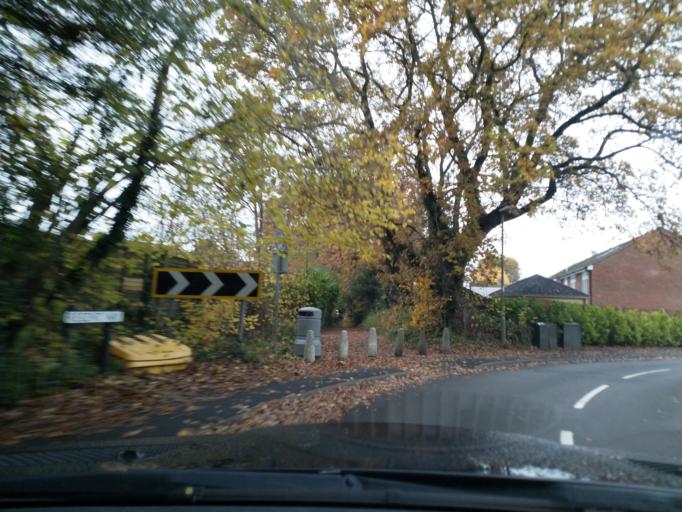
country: GB
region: England
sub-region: Surrey
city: Frimley
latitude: 51.3160
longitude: -0.7253
